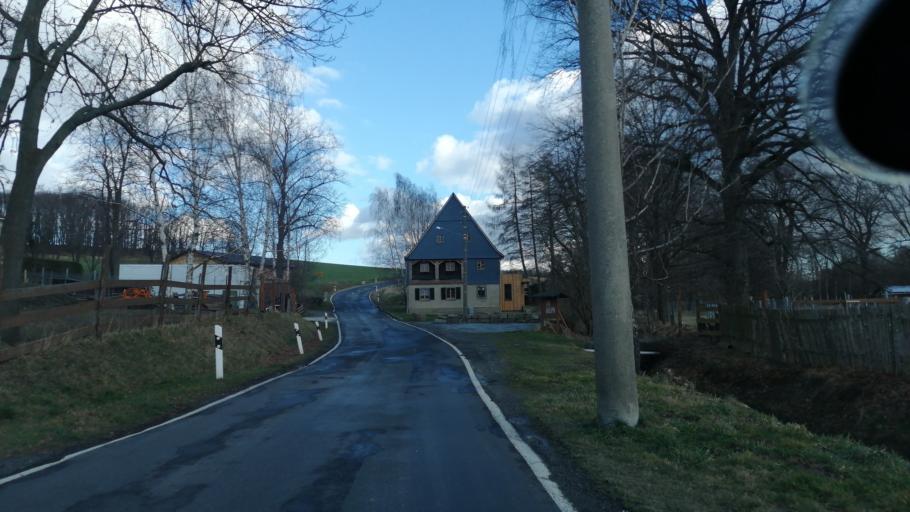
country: DE
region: Saxony
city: Kubschutz
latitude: 51.1437
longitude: 14.5381
